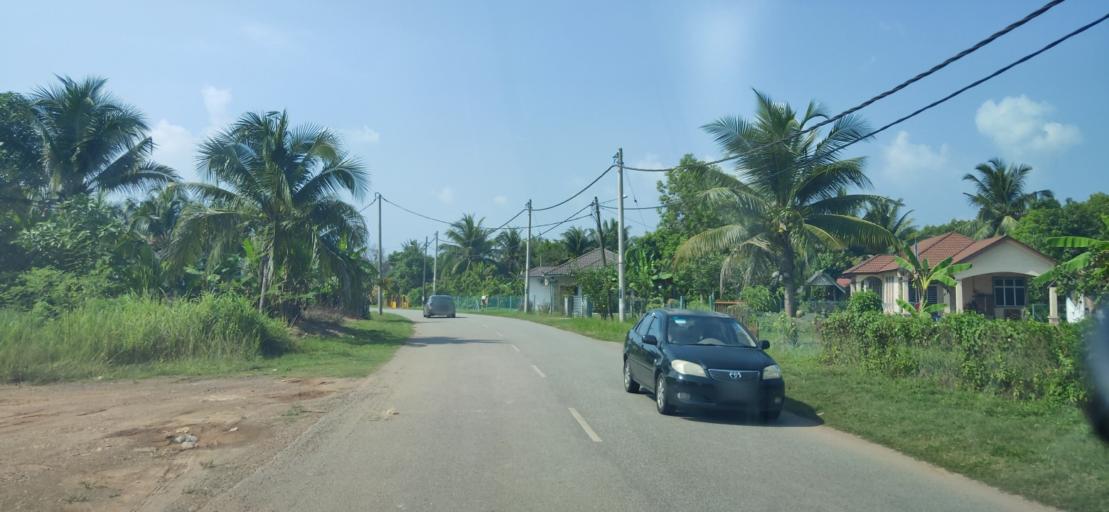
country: MY
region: Kedah
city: Sungai Petani
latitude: 5.6559
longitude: 100.4619
